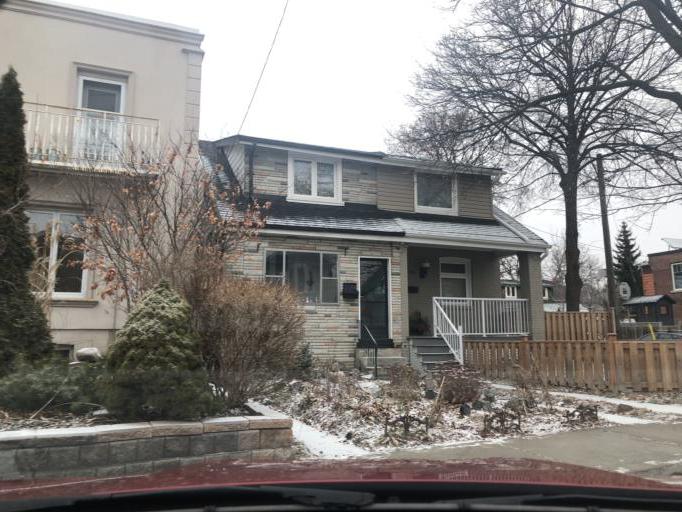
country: CA
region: Ontario
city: Toronto
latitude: 43.6737
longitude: -79.3348
